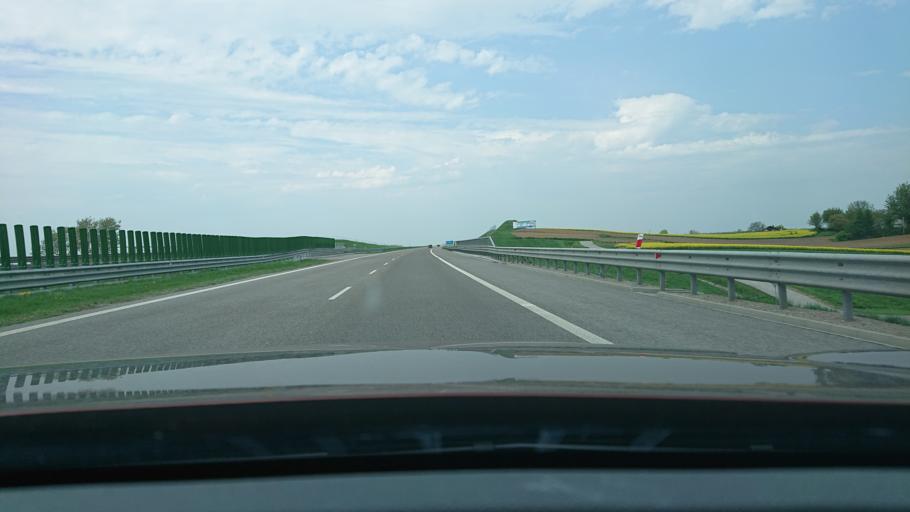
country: PL
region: Subcarpathian Voivodeship
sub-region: Powiat jaroslawski
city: Pawlosiow
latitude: 49.9519
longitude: 22.6626
